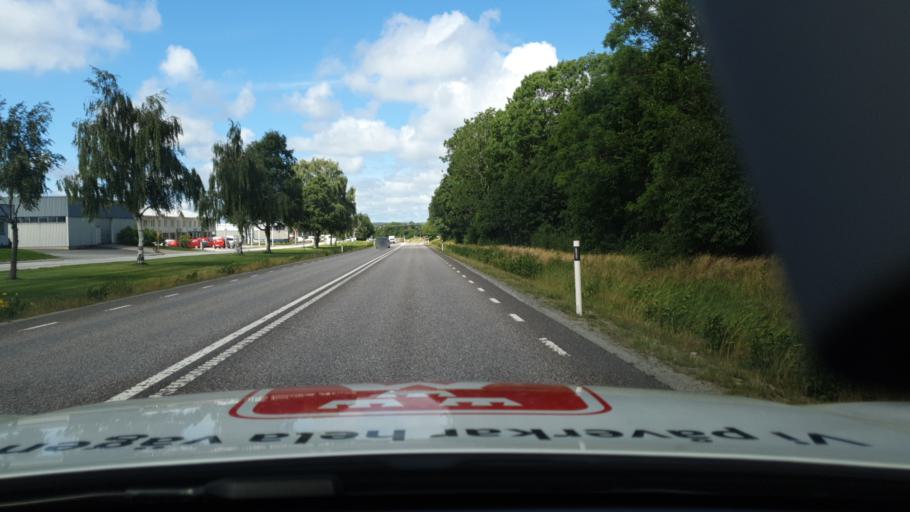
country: SE
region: Vaestra Goetaland
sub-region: Stenungsunds Kommun
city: Stenungsund
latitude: 58.0734
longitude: 11.8451
